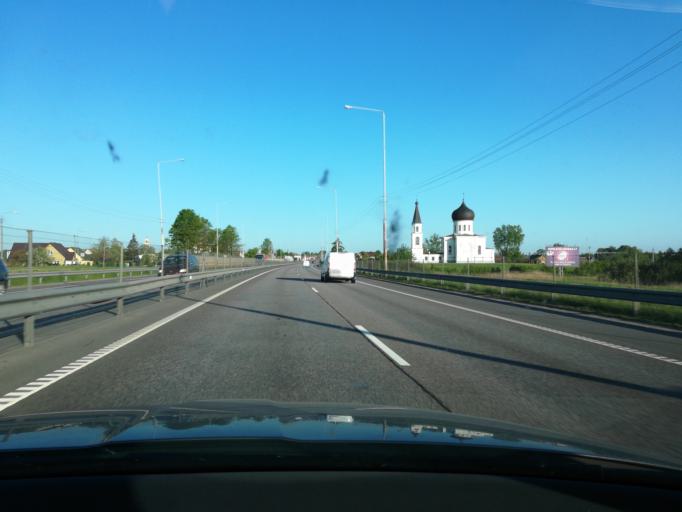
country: LT
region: Vilnius County
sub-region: Vilniaus Rajonas
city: Vievis
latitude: 54.7695
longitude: 24.8295
